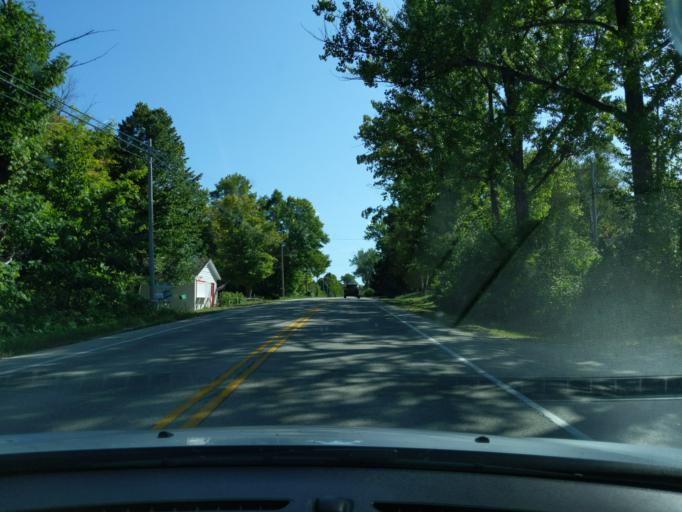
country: US
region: Michigan
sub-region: Delta County
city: Escanaba
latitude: 45.2791
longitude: -87.0194
